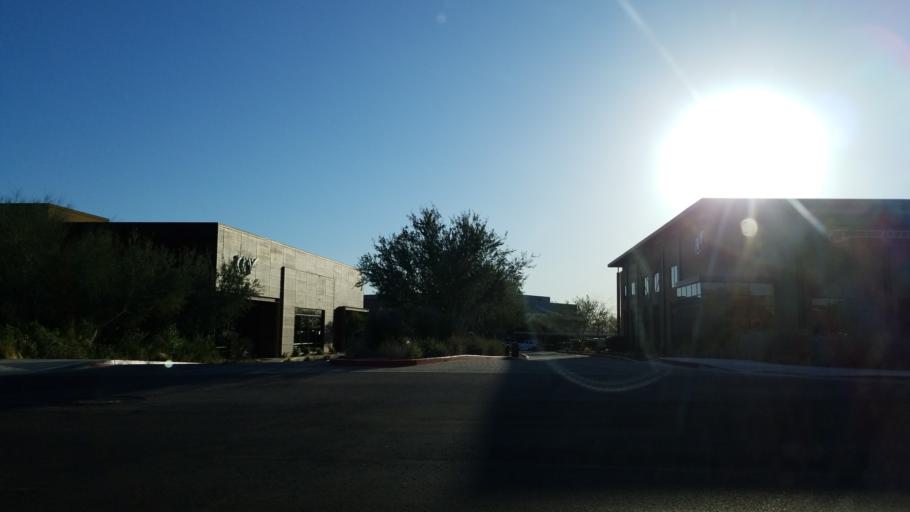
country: US
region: Arizona
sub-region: Maricopa County
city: Paradise Valley
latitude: 33.6586
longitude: -111.8892
